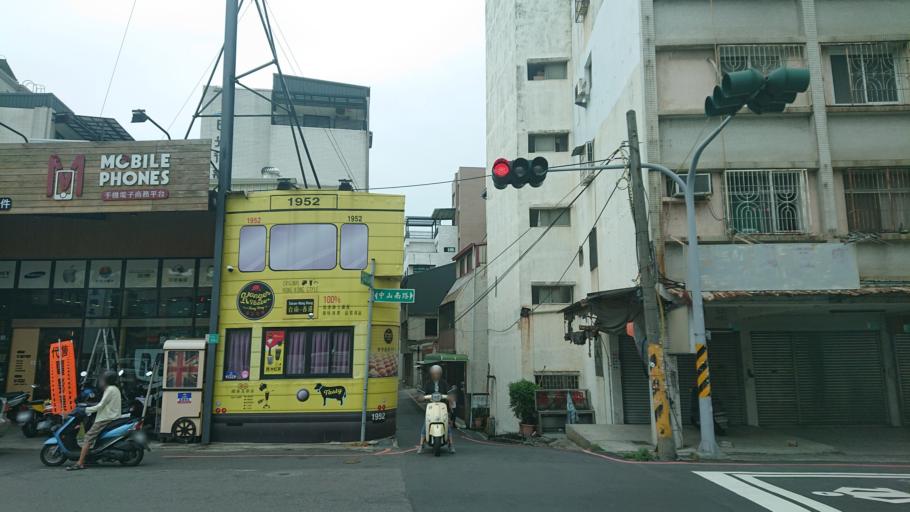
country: TW
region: Taiwan
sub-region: Tainan
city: Tainan
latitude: 23.0129
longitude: 120.2292
